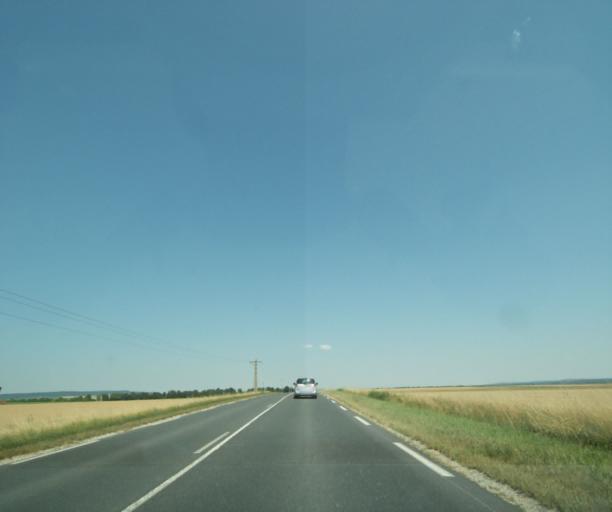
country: FR
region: Champagne-Ardenne
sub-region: Departement de la Marne
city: Mourmelon-le-Grand
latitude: 49.0822
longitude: 4.2812
